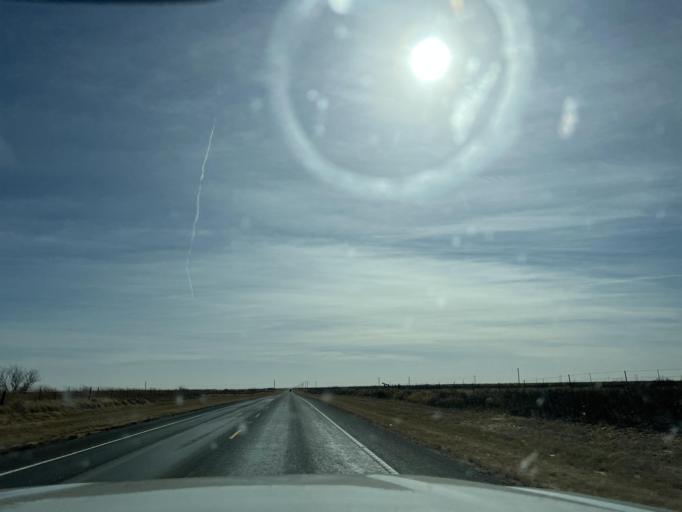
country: US
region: Texas
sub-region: Andrews County
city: Andrews
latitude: 32.4282
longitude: -102.4366
